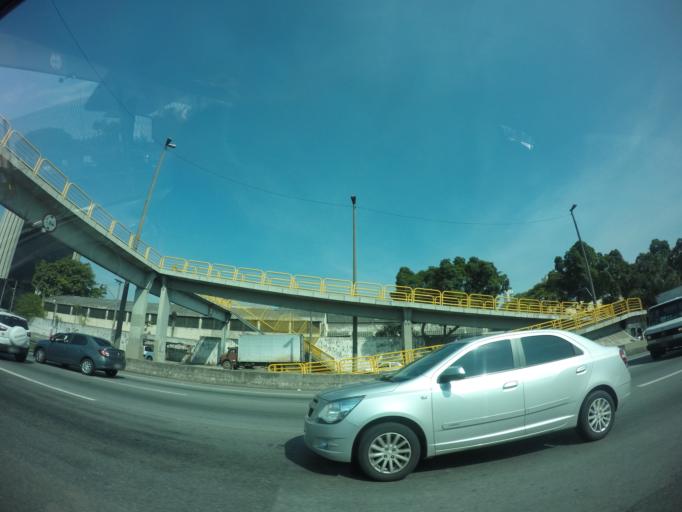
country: BR
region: Sao Paulo
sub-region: Sao Paulo
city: Sao Paulo
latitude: -23.5170
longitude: -46.5806
